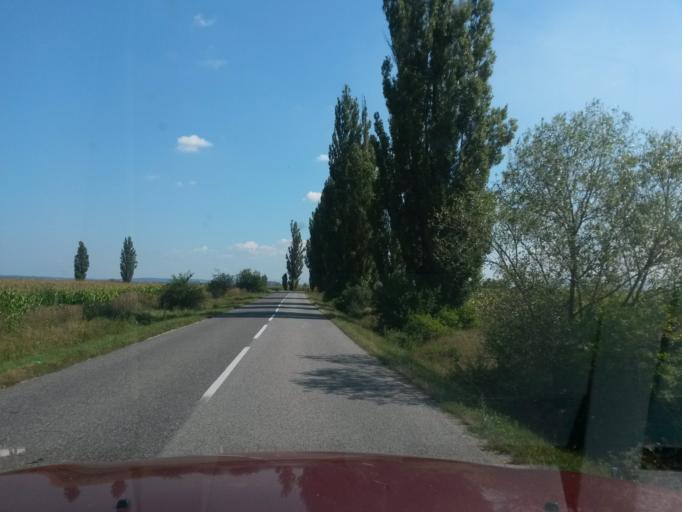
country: SK
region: Kosicky
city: Moldava nad Bodvou
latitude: 48.5478
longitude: 21.0823
